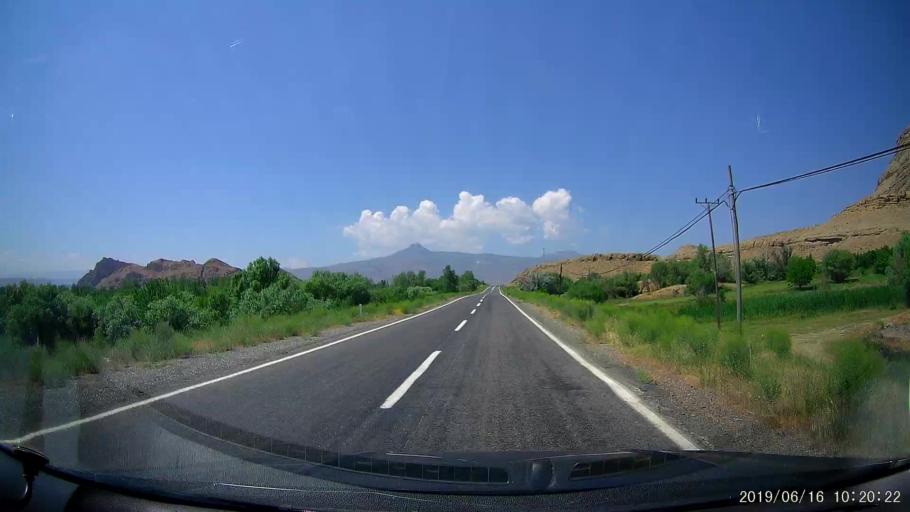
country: TR
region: Igdir
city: Tuzluca
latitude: 40.1484
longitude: 43.6484
